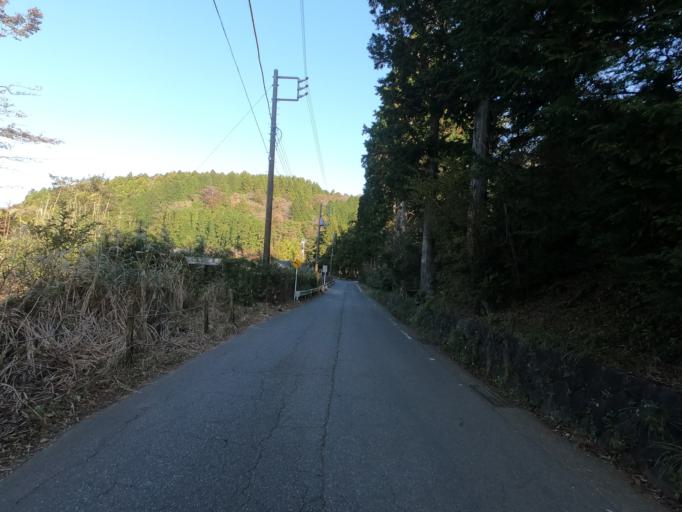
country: JP
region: Kanagawa
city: Hakone
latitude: 35.2069
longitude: 139.0171
